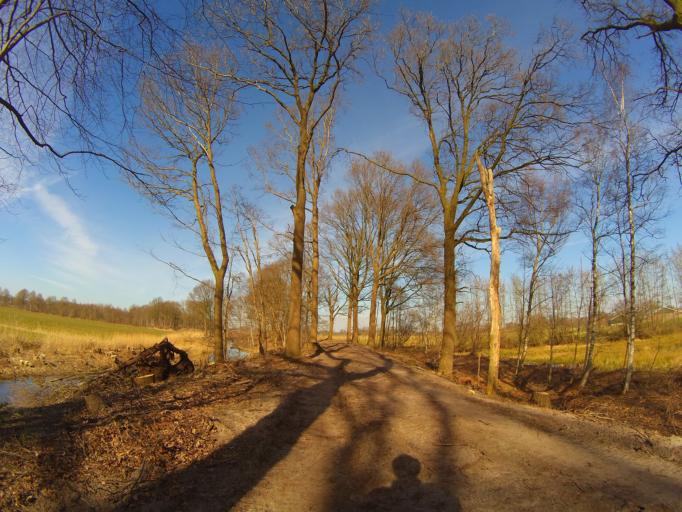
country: NL
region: Gelderland
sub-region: Gemeente Ede
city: Ederveen
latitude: 52.0779
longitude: 5.5625
